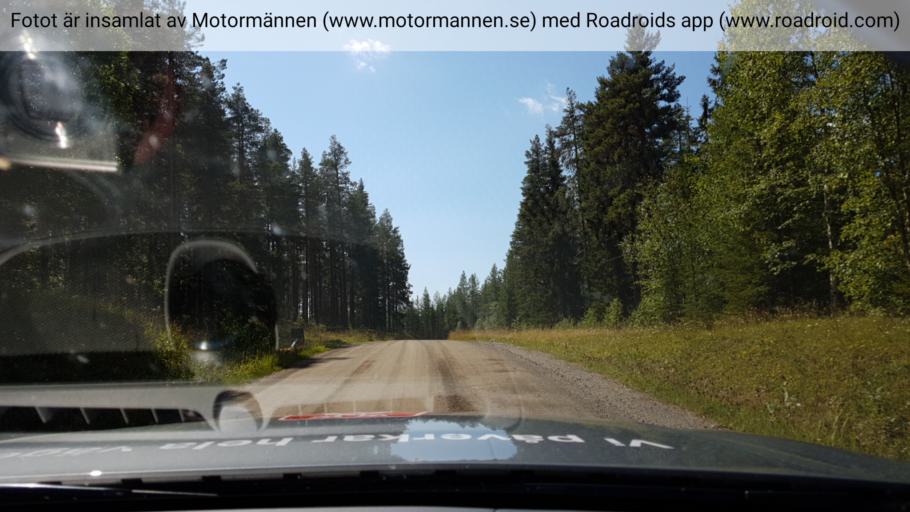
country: SE
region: Jaemtland
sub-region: Stroemsunds Kommun
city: Stroemsund
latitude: 63.3281
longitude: 15.4661
